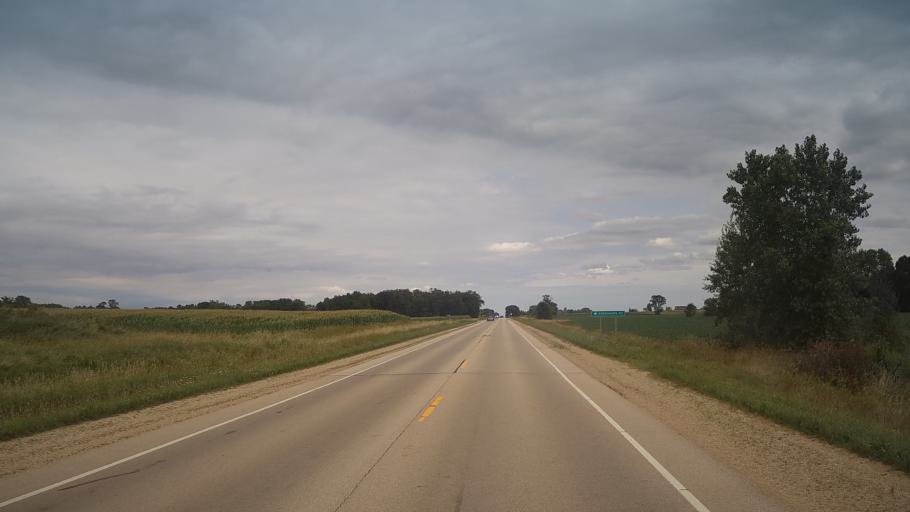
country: US
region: Wisconsin
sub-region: Green Lake County
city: Berlin
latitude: 44.0488
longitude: -88.9496
